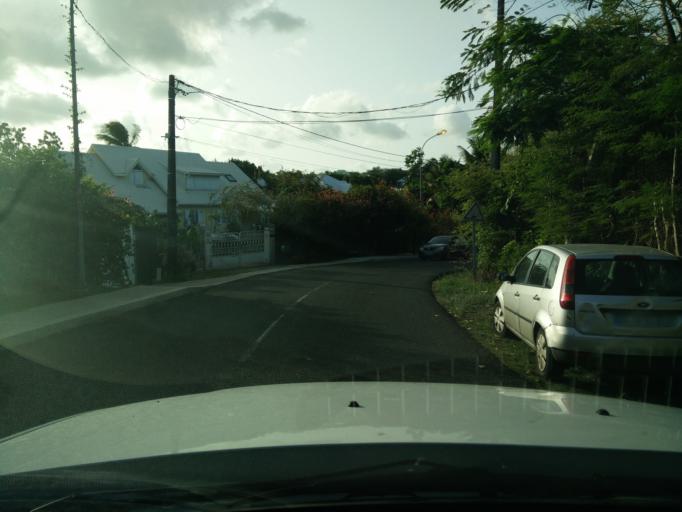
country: GP
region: Guadeloupe
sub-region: Guadeloupe
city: Le Gosier
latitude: 16.2025
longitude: -61.4720
